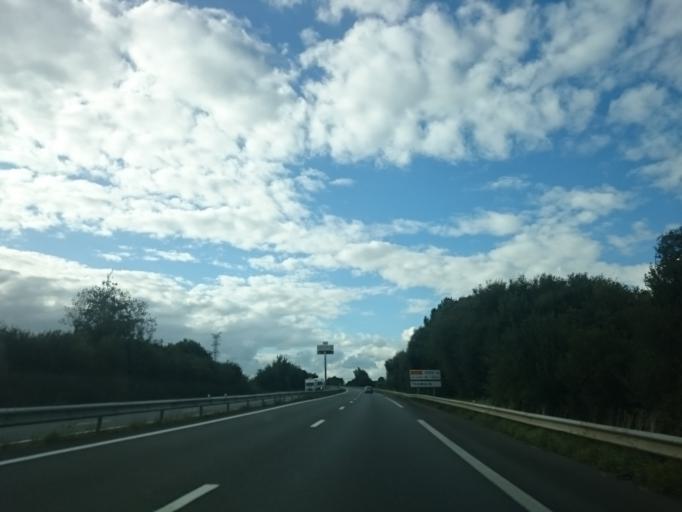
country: FR
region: Brittany
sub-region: Departement des Cotes-d'Armor
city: Plenee-Jugon
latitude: 48.3849
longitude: -2.3800
